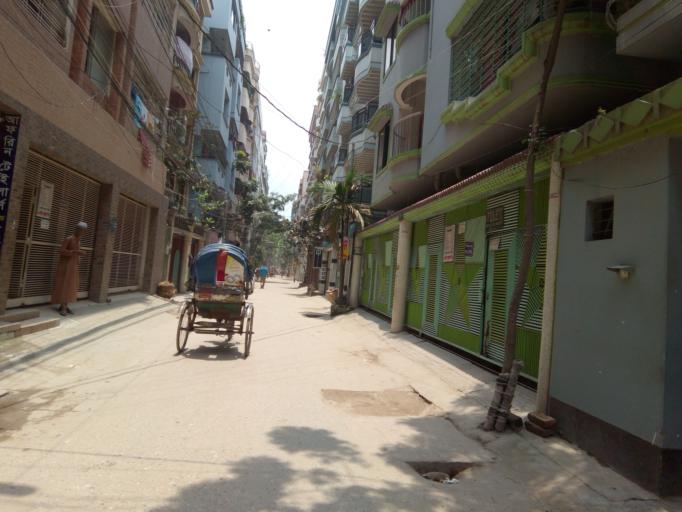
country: BD
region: Dhaka
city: Paltan
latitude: 23.7630
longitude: 90.4288
